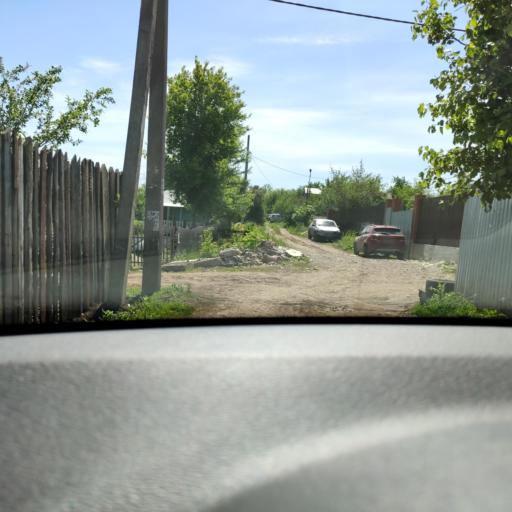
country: RU
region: Samara
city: Petra-Dubrava
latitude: 53.2925
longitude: 50.2986
